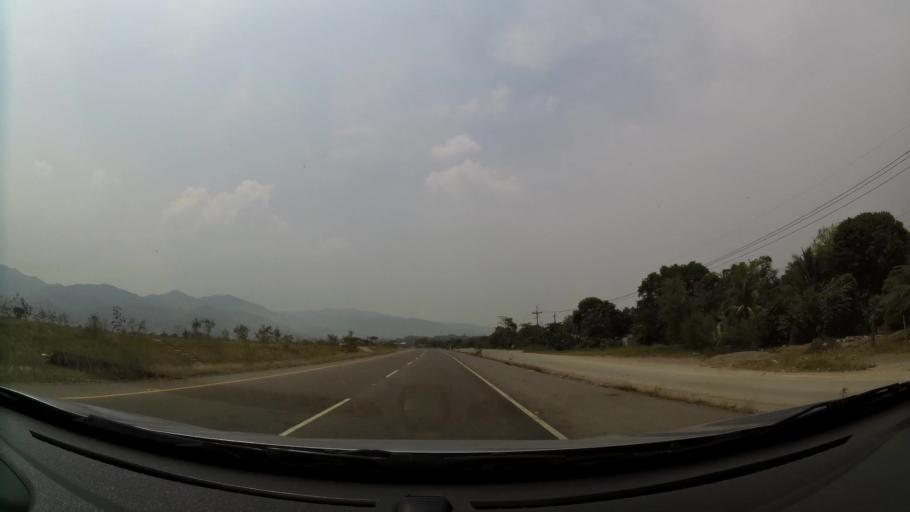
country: HN
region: Cortes
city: El Plan
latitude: 15.2937
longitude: -87.9792
